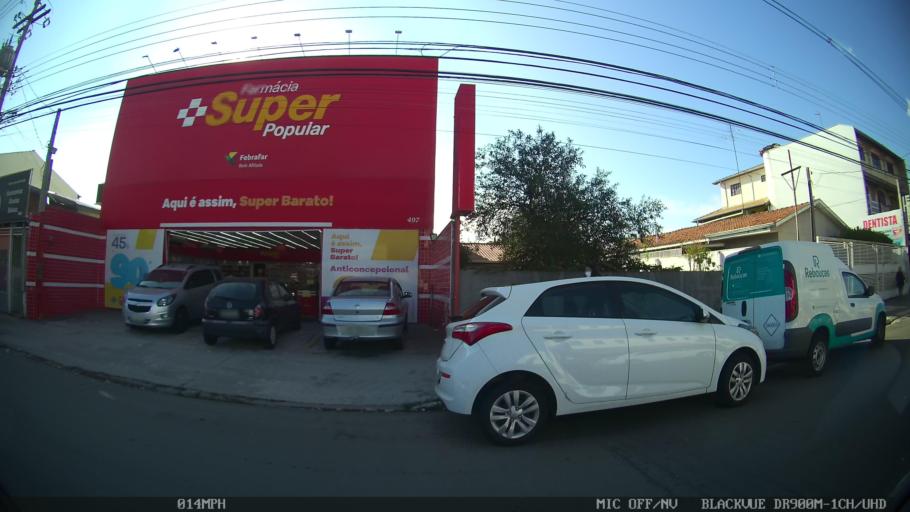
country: BR
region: Sao Paulo
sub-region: Hortolandia
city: Hortolandia
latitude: -22.8971
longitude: -47.1745
